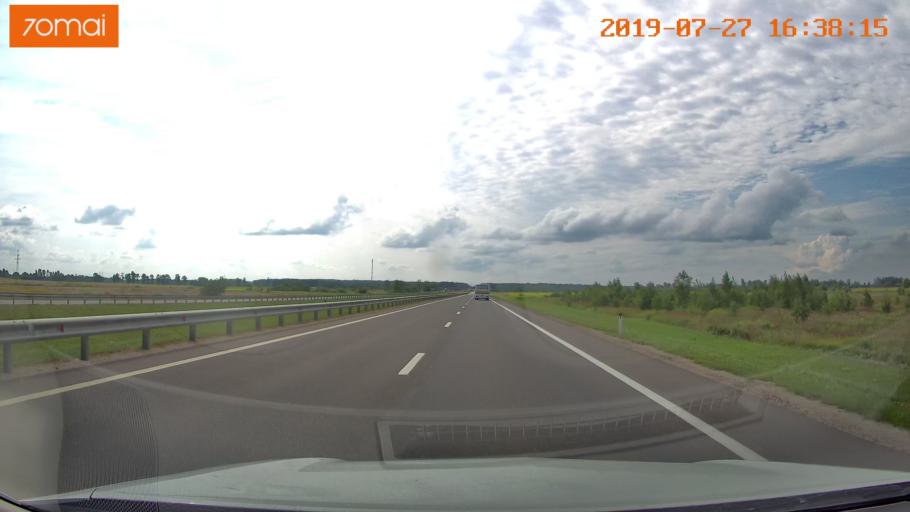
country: RU
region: Kaliningrad
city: Gvardeysk
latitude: 54.6488
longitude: 21.2335
